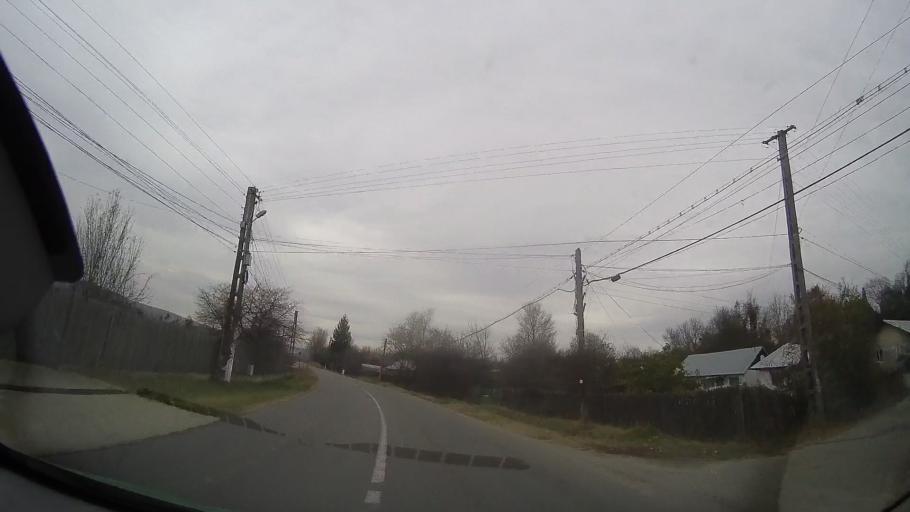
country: RO
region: Prahova
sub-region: Comuna Iordachianu
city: Iordacheanu
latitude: 45.0332
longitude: 26.2408
